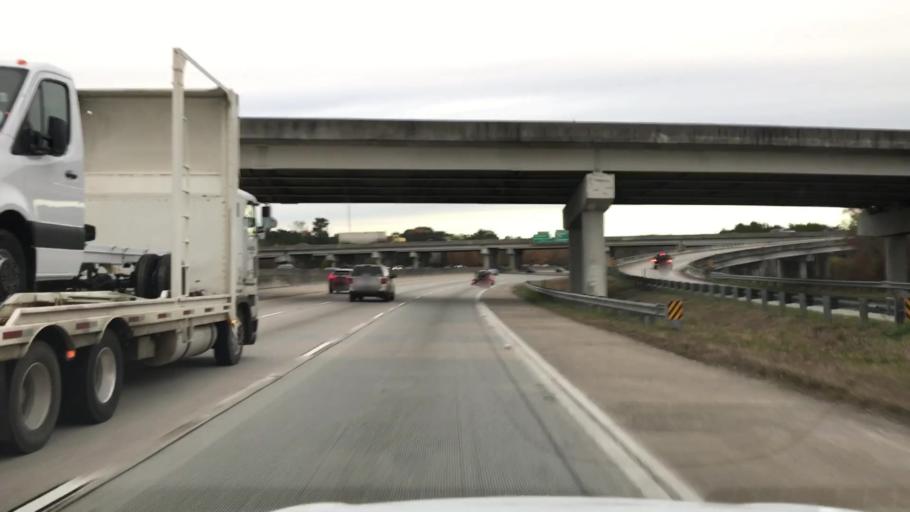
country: US
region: South Carolina
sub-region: Berkeley County
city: Hanahan
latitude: 32.8816
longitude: -80.0186
